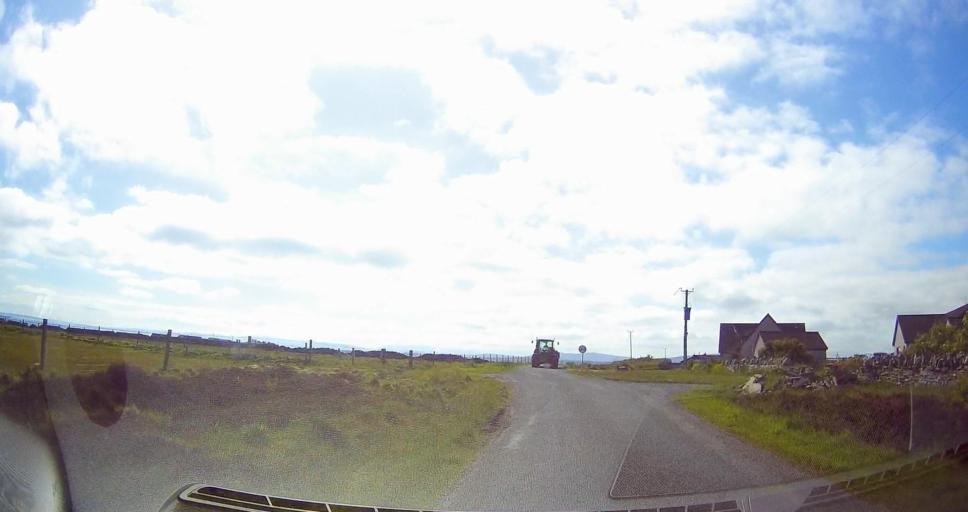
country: GB
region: Scotland
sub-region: Orkney Islands
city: Kirkwall
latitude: 58.9628
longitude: -2.9522
